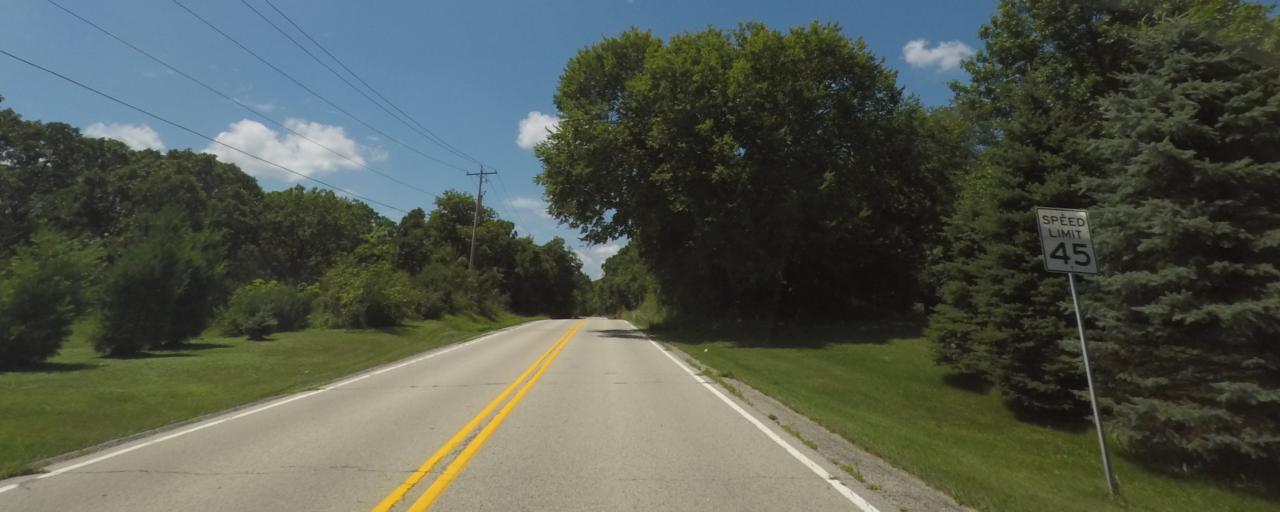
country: US
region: Wisconsin
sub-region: Waukesha County
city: Wales
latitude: 42.9954
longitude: -88.3914
